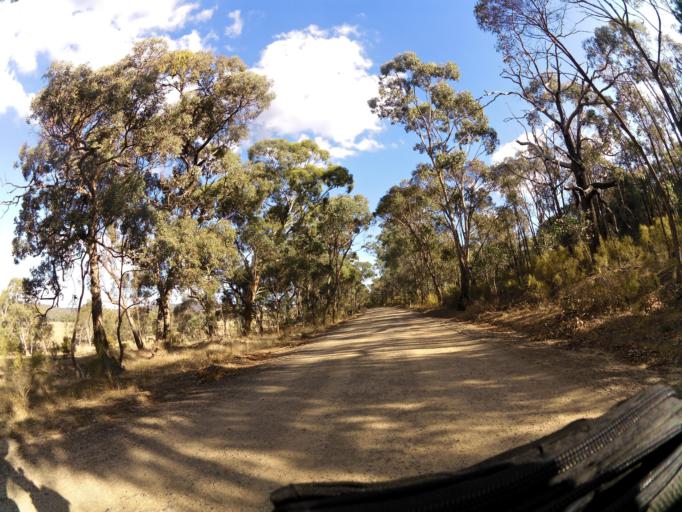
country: AU
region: Victoria
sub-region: Greater Bendigo
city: Kennington
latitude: -37.0142
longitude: 144.8081
